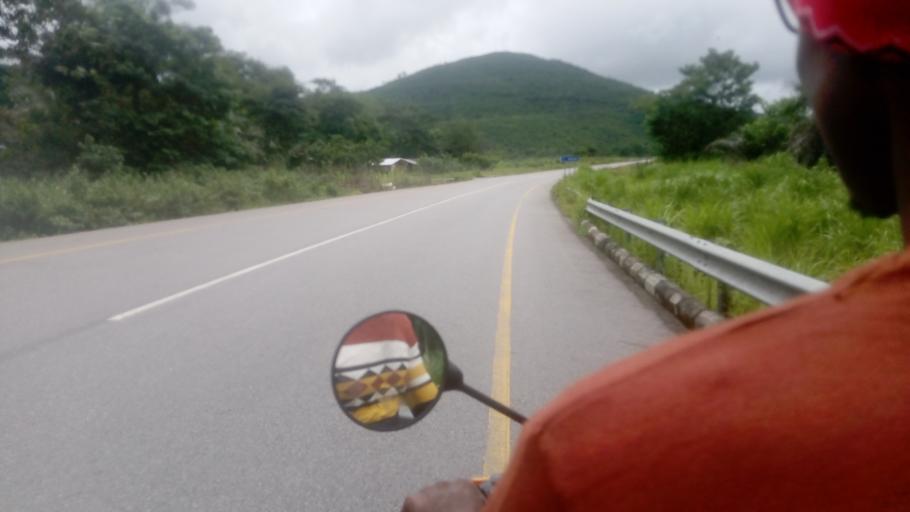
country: SL
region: Northern Province
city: Masaka
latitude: 8.6615
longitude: -11.8008
